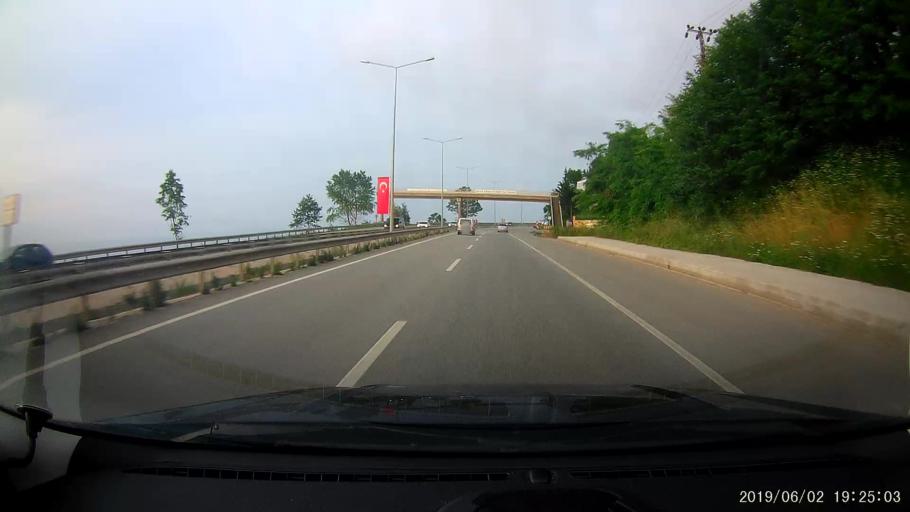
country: TR
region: Giresun
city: Bulancak
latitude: 40.9440
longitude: 38.2603
